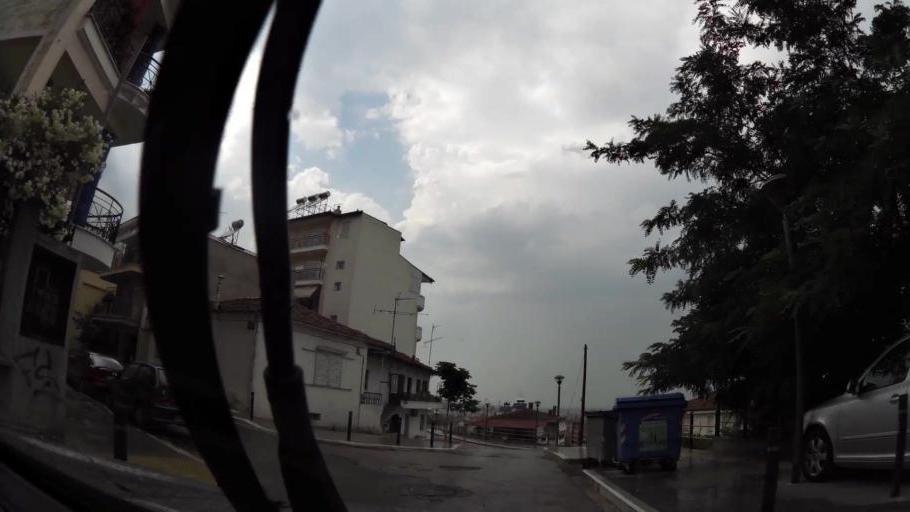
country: GR
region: Central Macedonia
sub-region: Nomos Imathias
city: Veroia
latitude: 40.5301
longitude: 22.2045
